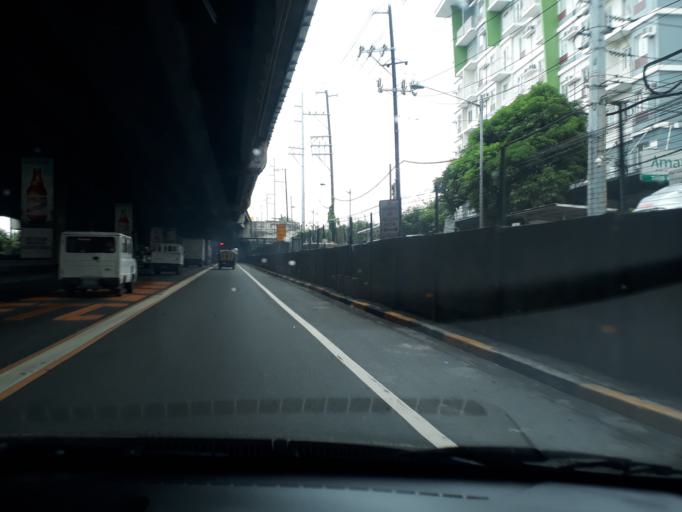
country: PH
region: Calabarzon
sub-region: Province of Rizal
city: Taguig
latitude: 14.4941
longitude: 121.0417
